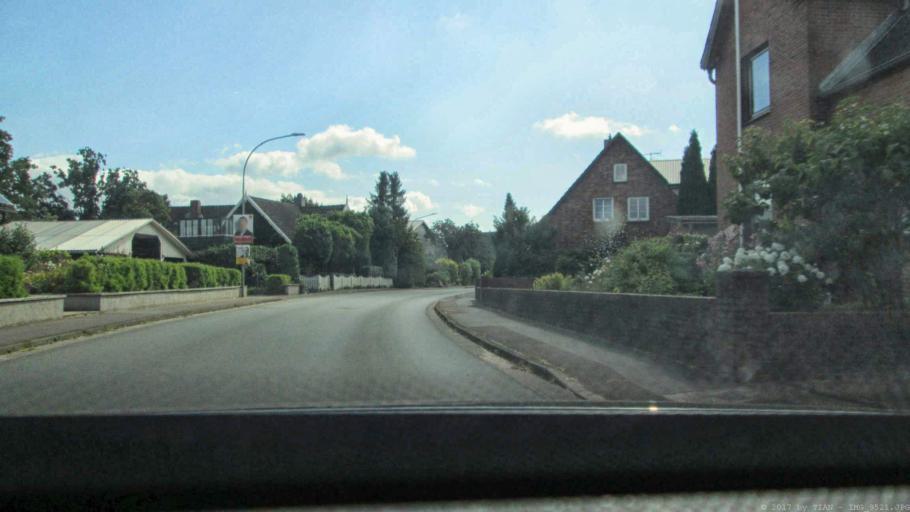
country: DE
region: Schleswig-Holstein
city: Seth
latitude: 53.8432
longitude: 10.1777
